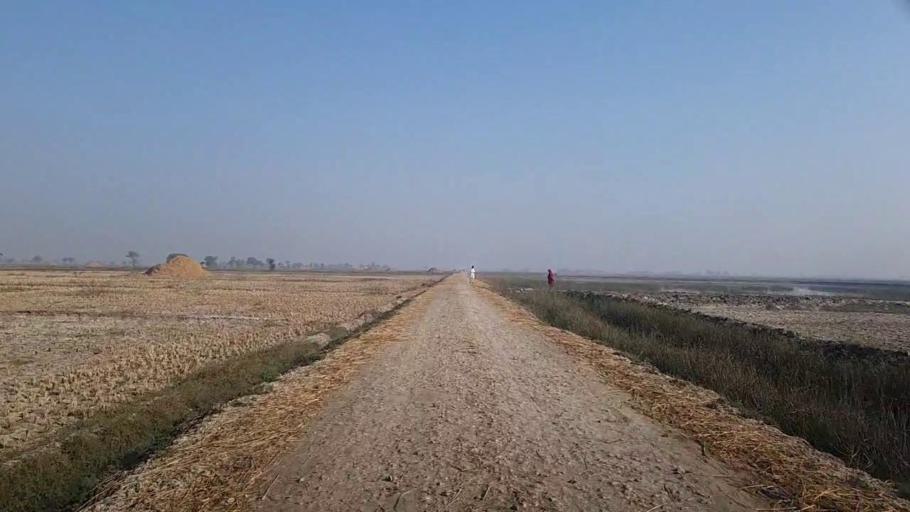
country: PK
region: Sindh
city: Radhan
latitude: 27.1356
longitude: 67.9051
